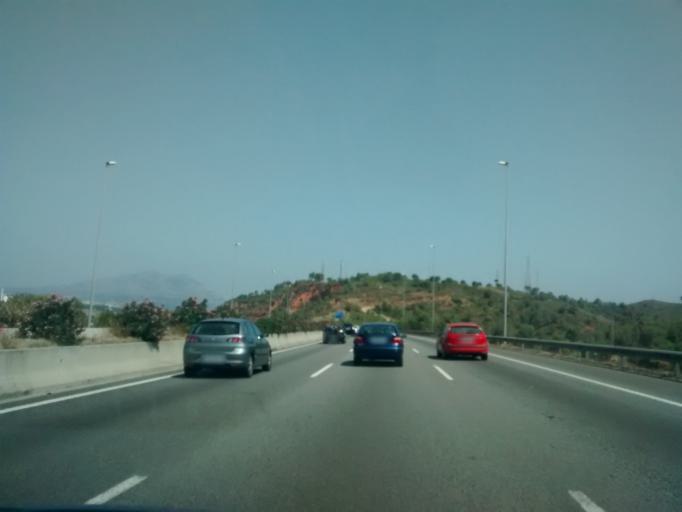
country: ES
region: Catalonia
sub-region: Provincia de Barcelona
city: Martorell
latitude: 41.4823
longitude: 1.9358
